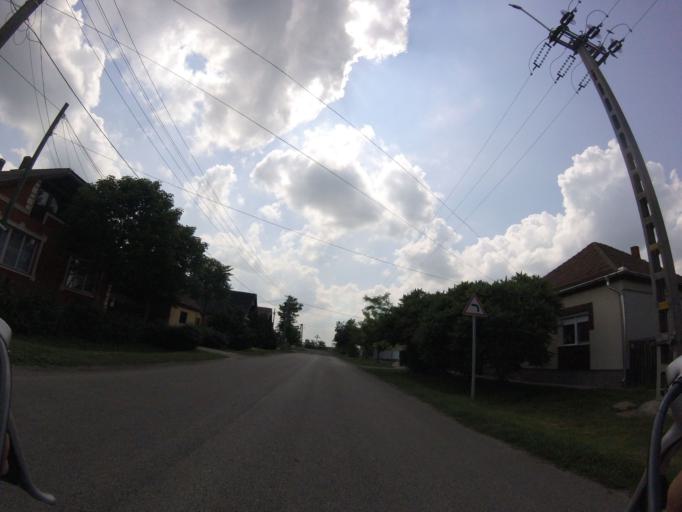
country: HU
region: Heves
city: Tiszanana
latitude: 47.5976
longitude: 20.4364
